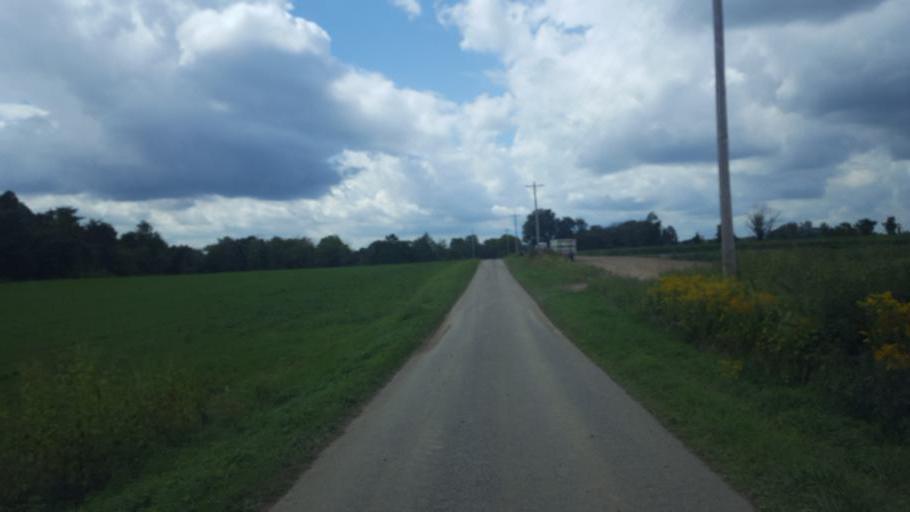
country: US
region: Ohio
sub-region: Huron County
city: Plymouth
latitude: 41.0783
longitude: -82.6329
